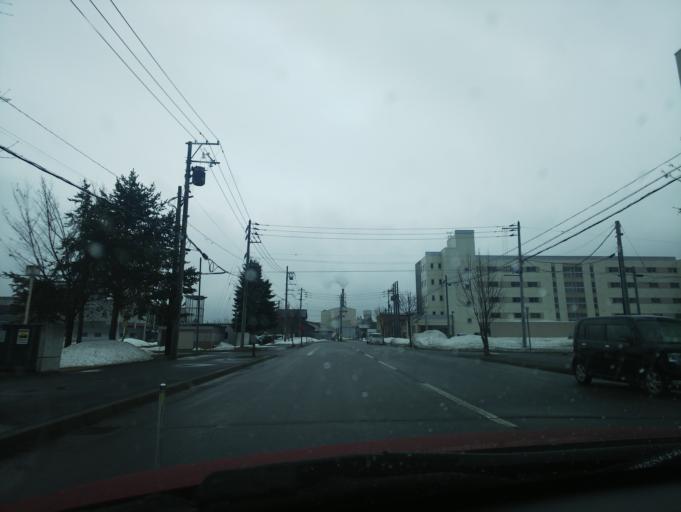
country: JP
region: Hokkaido
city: Nayoro
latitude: 44.3440
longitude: 142.4605
